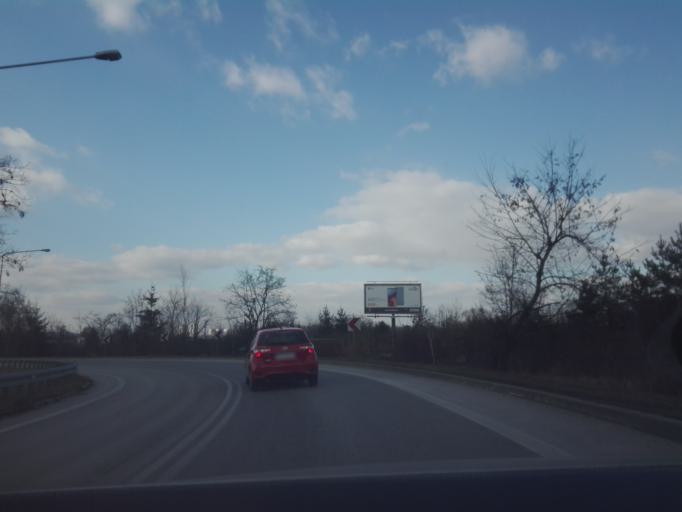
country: PL
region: Silesian Voivodeship
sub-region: Katowice
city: Katowice
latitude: 50.2535
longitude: 18.9862
